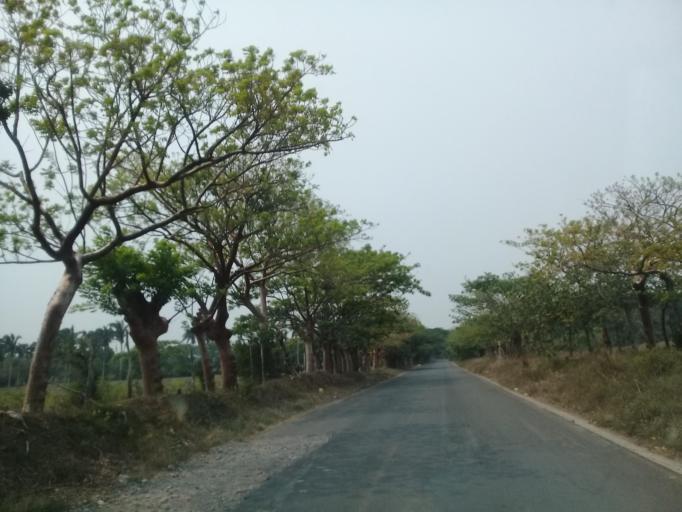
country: MX
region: Veracruz
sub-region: Medellin
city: La Laguna y Monte del Castillo
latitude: 18.9636
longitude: -96.1210
